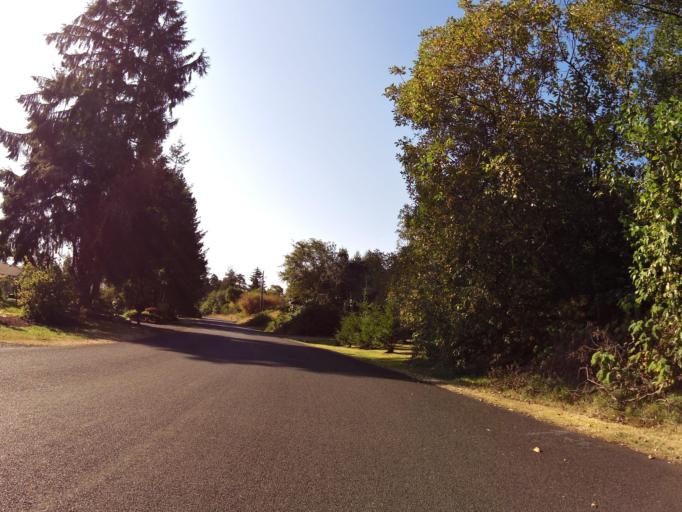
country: US
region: Oregon
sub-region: Clatsop County
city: Warrenton
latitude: 46.1350
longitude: -123.9340
